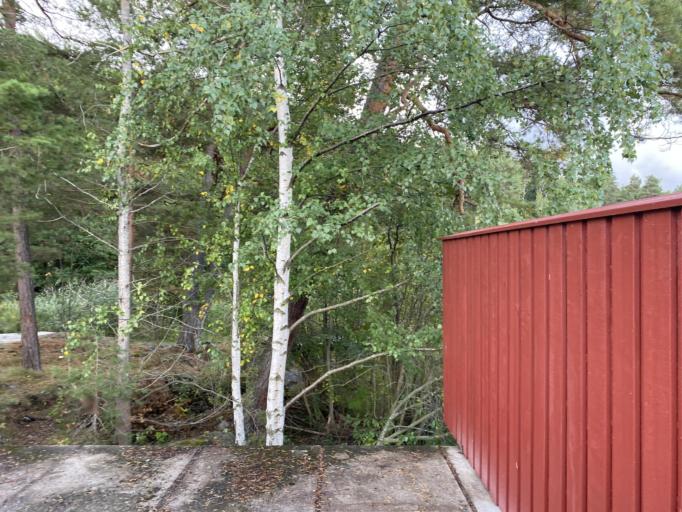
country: SE
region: Stockholm
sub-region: Salems Kommun
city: Ronninge
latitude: 59.1870
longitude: 17.7091
